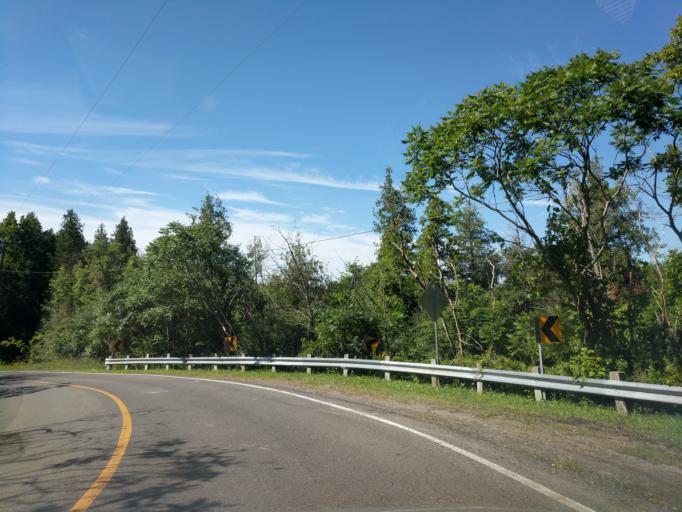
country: CA
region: Ontario
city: Pickering
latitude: 43.8362
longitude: -79.1829
